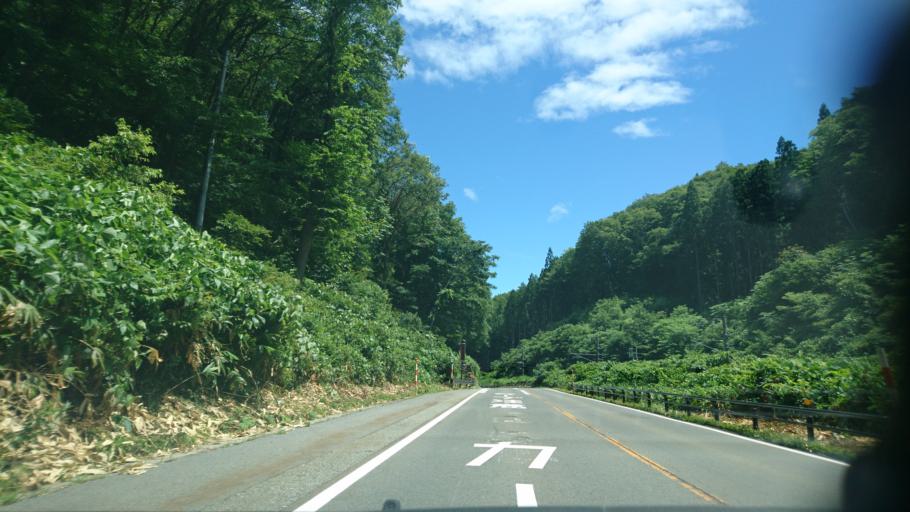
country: JP
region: Akita
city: Kakunodatemachi
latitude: 39.6752
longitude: 140.6986
